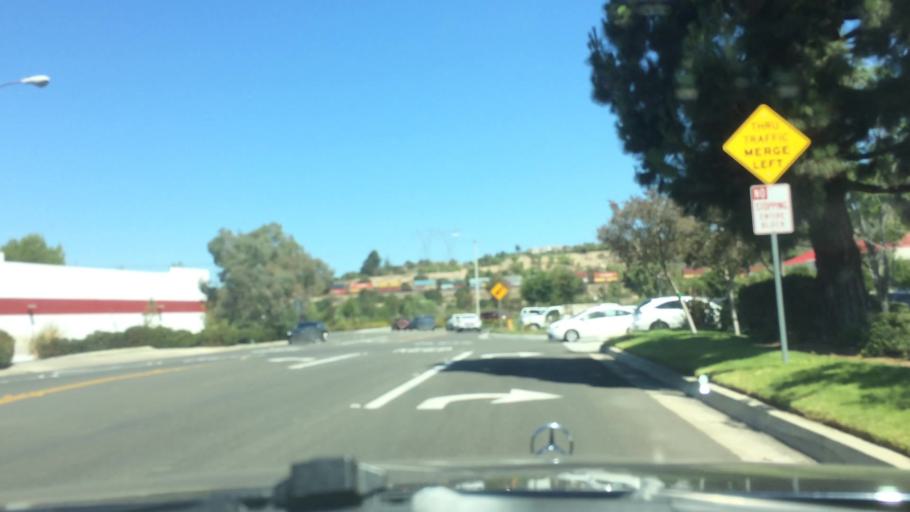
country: US
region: California
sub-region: Orange County
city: Yorba Linda
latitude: 33.8747
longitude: -117.7450
